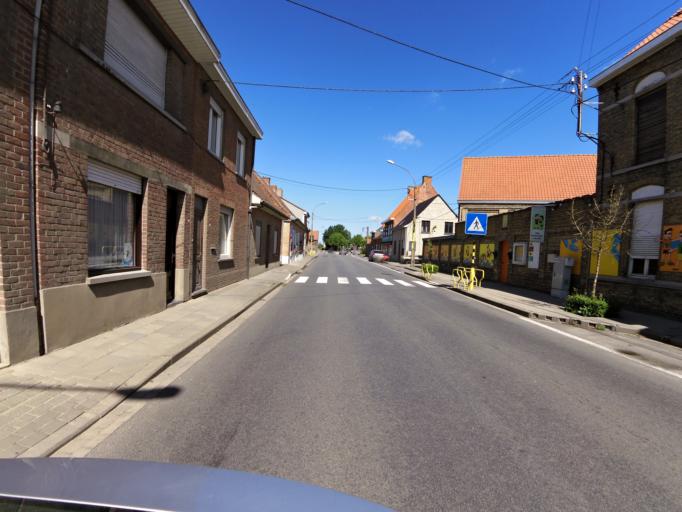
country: BE
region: Flanders
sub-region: Provincie West-Vlaanderen
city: Ieper
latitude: 50.8686
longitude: 2.8468
